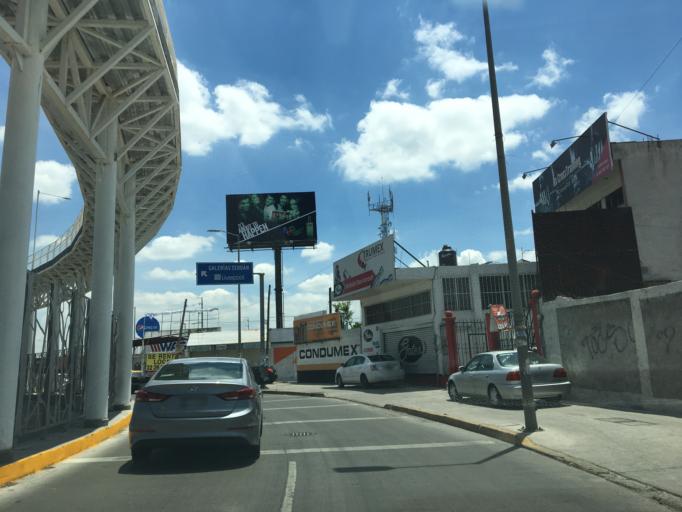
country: MX
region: Puebla
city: Puebla
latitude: 19.0579
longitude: -98.2192
